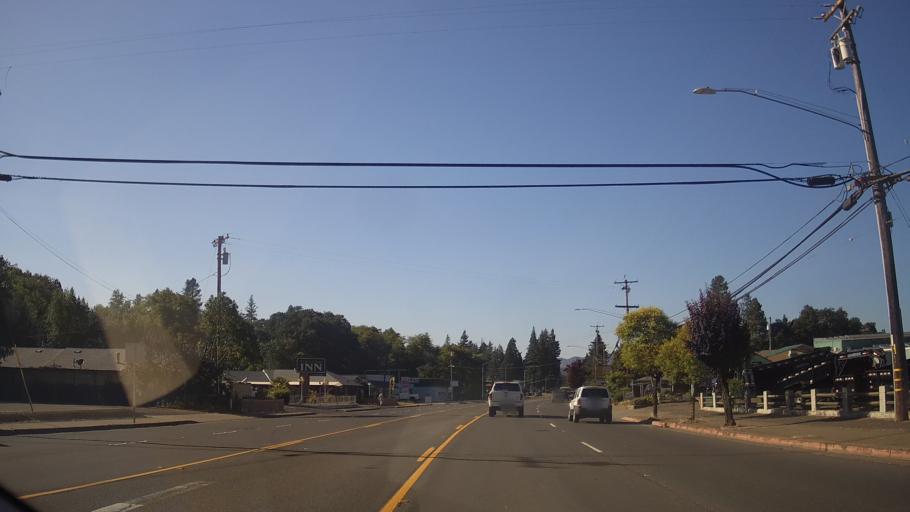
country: US
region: California
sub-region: Mendocino County
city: Willits
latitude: 39.3956
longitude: -123.3492
